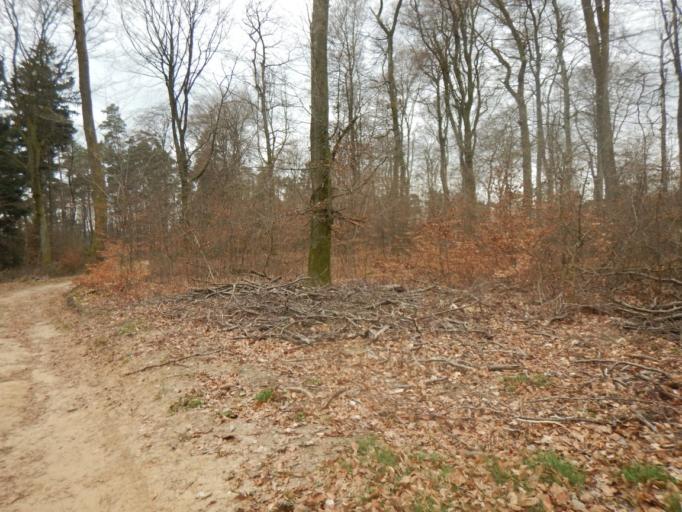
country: LU
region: Luxembourg
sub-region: Canton de Mersch
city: Lorentzweiler
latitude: 49.6947
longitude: 6.1539
